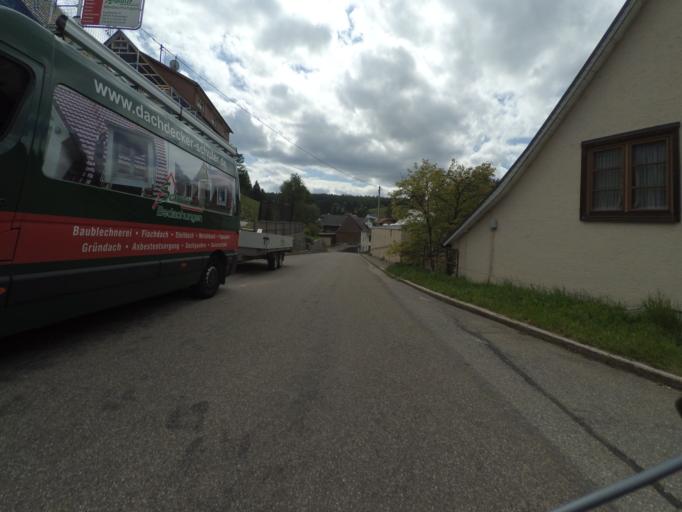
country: DE
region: Baden-Wuerttemberg
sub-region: Freiburg Region
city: Eisenbach
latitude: 47.9652
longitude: 8.2966
